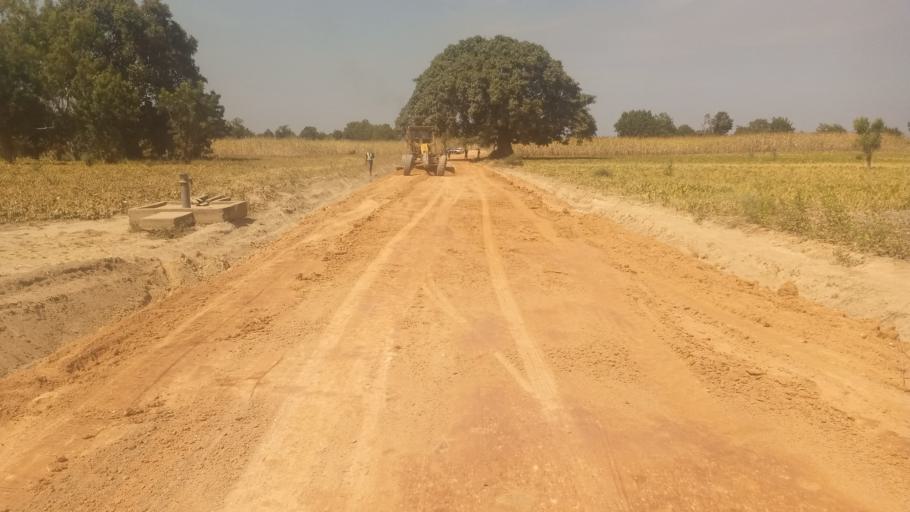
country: NG
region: Adamawa
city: Madagali
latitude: 10.8377
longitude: 13.3994
